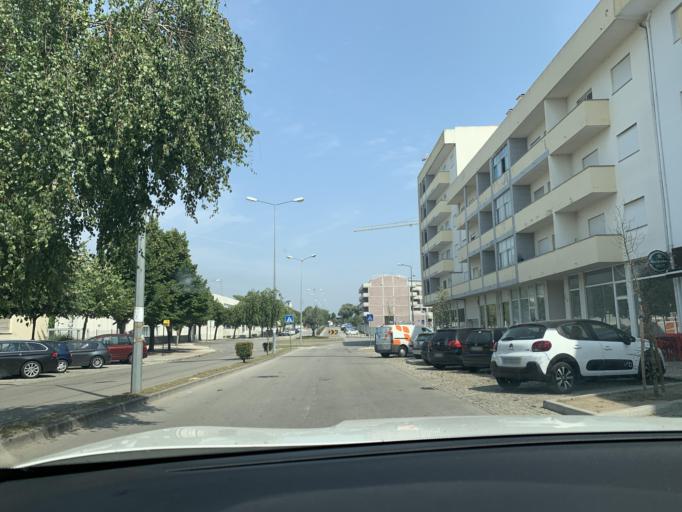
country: PT
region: Viseu
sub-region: Viseu
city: Viseu
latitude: 40.6458
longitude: -7.9183
